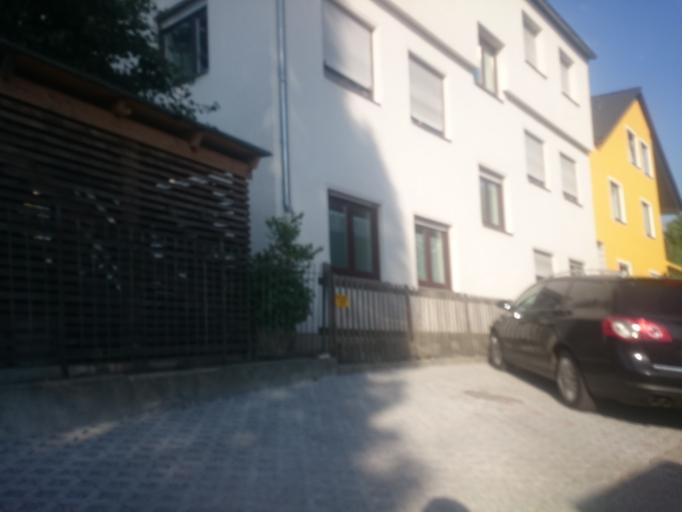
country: DE
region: Bavaria
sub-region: Swabia
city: Augsburg
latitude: 48.3726
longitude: 10.8828
